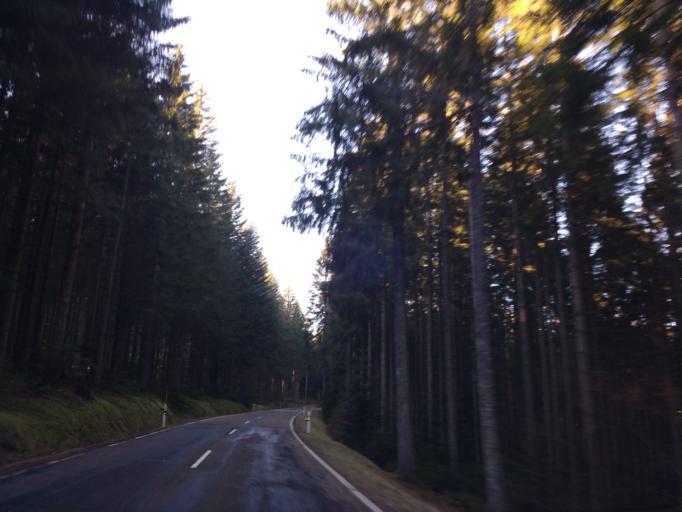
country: DE
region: Baden-Wuerttemberg
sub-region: Karlsruhe Region
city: Bad Rippoldsau-Schapbach
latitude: 48.4429
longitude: 8.3621
